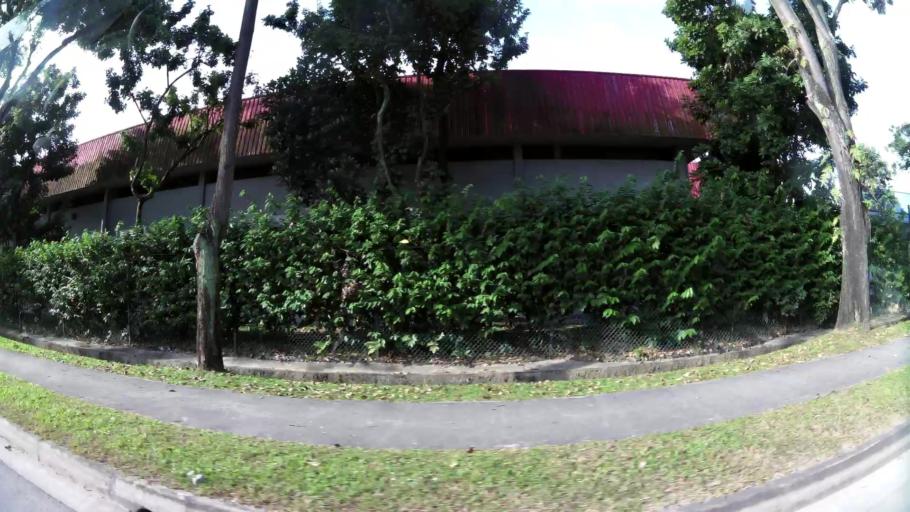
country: MY
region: Johor
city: Johor Bahru
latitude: 1.3257
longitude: 103.6566
